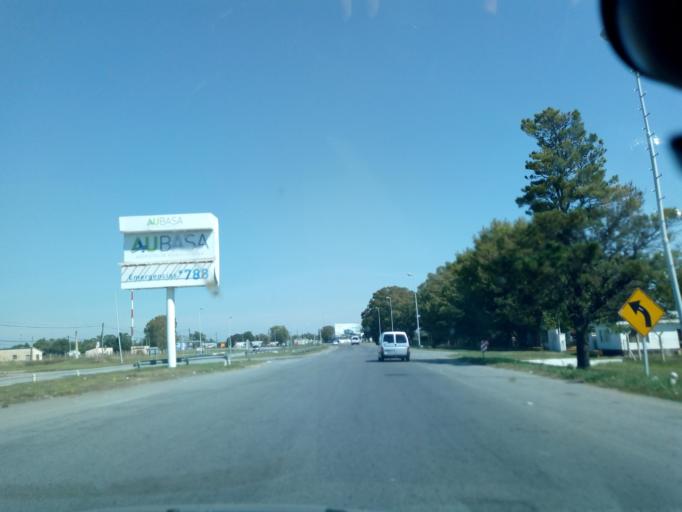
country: AR
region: Buenos Aires
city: Maipu
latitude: -36.8481
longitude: -57.8683
